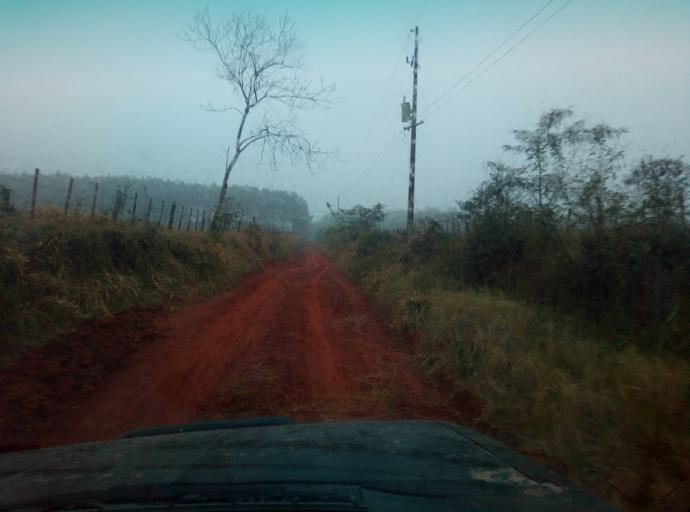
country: PY
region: Caaguazu
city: Doctor Cecilio Baez
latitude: -25.1613
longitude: -56.2619
